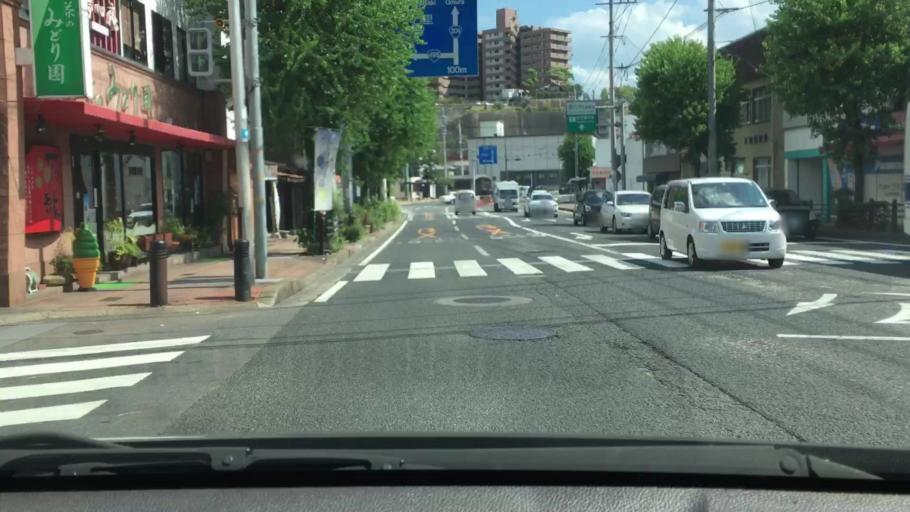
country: JP
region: Nagasaki
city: Sasebo
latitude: 33.2073
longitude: 129.7208
